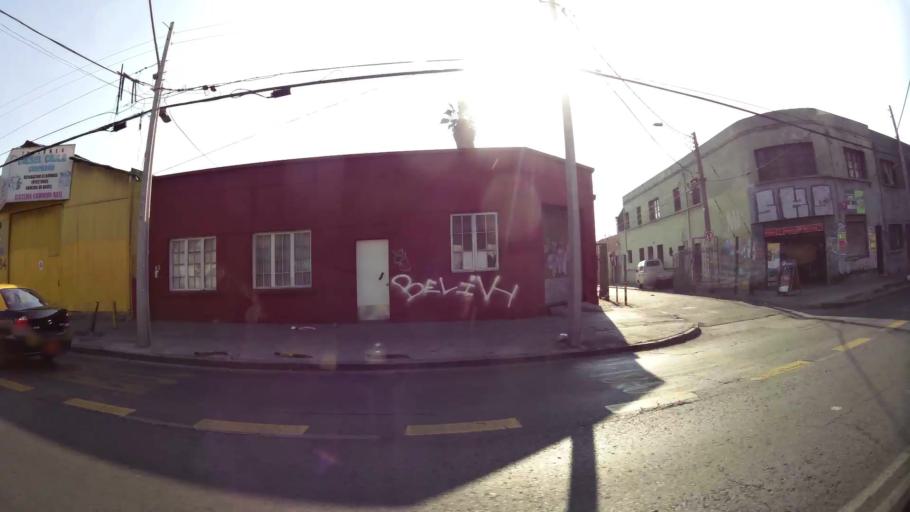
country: CL
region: Santiago Metropolitan
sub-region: Provincia de Santiago
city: Santiago
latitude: -33.4096
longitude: -70.6434
